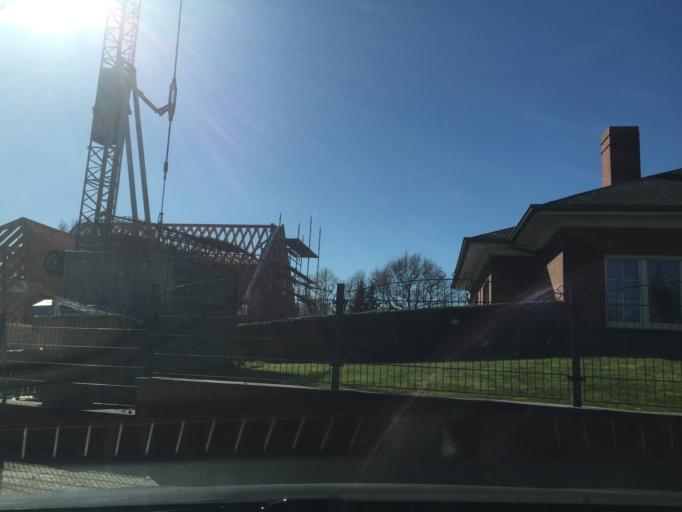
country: BE
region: Flanders
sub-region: Provincie West-Vlaanderen
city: Hooglede
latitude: 50.9800
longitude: 3.0707
